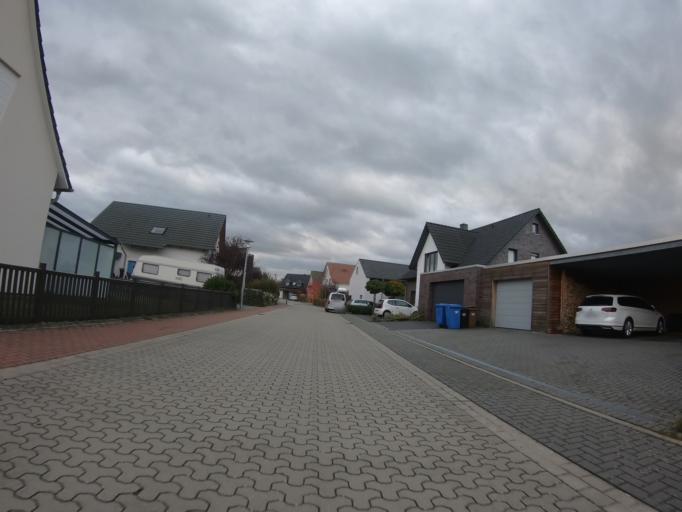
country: DE
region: Lower Saxony
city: Isenbuttel
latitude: 52.4419
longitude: 10.5766
